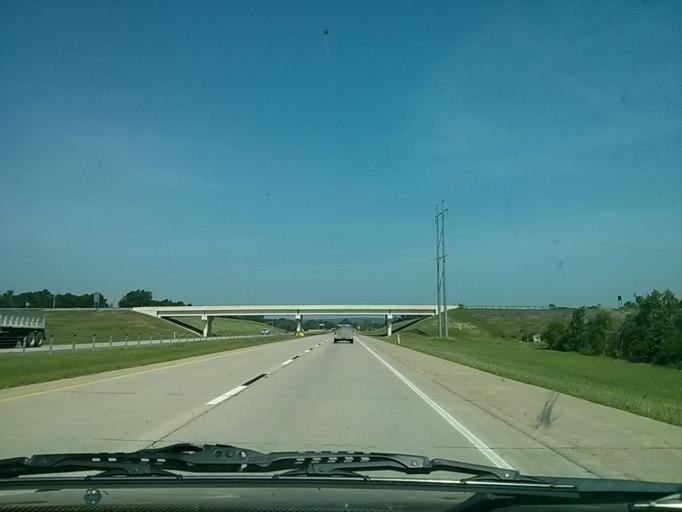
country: US
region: Oklahoma
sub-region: Creek County
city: Sapulpa
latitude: 36.0177
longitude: -96.0643
